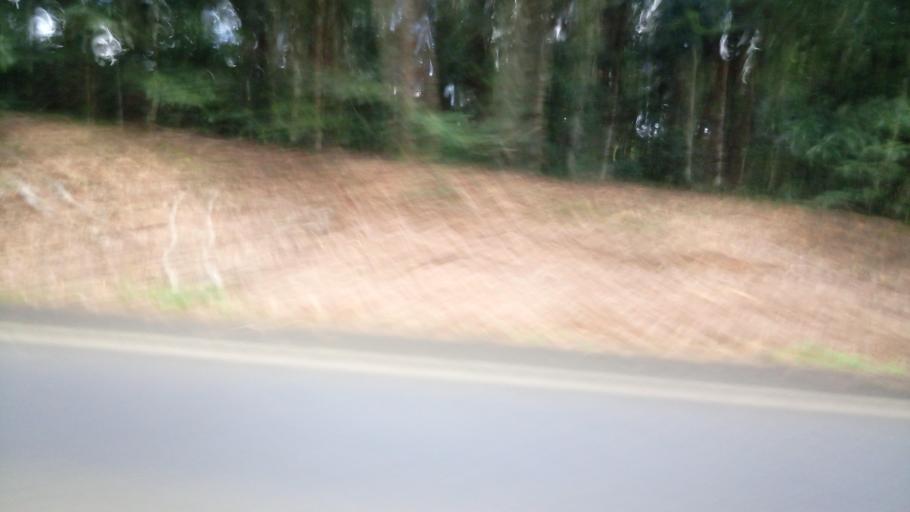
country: AU
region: Queensland
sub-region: Tablelands
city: Tolga
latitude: -17.2439
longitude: 145.6420
